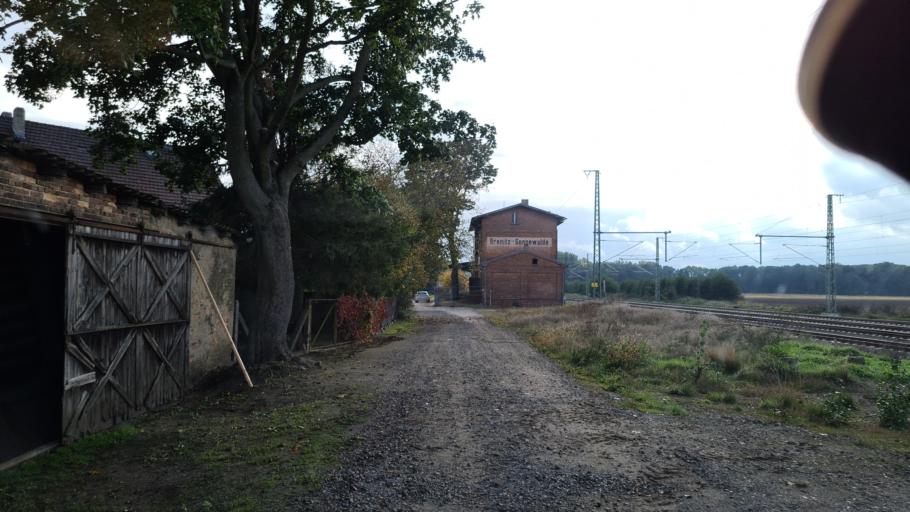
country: DE
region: Brandenburg
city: Schonewalde
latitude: 51.7018
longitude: 13.5968
